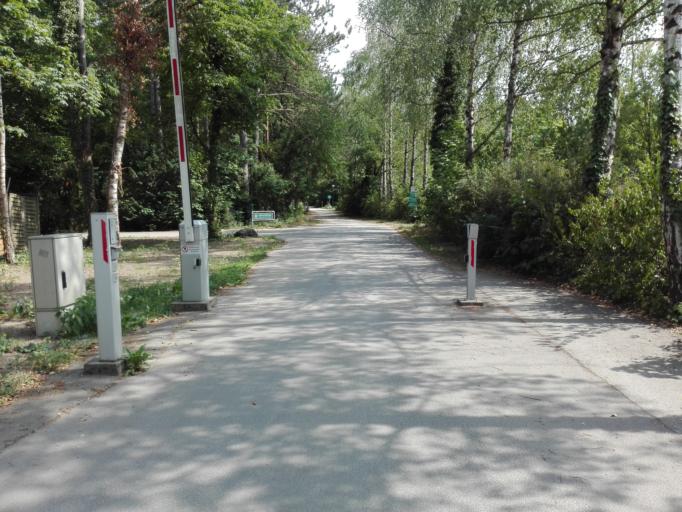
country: AT
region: Upper Austria
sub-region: Politischer Bezirk Linz-Land
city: Traun
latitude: 48.2386
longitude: 14.2461
